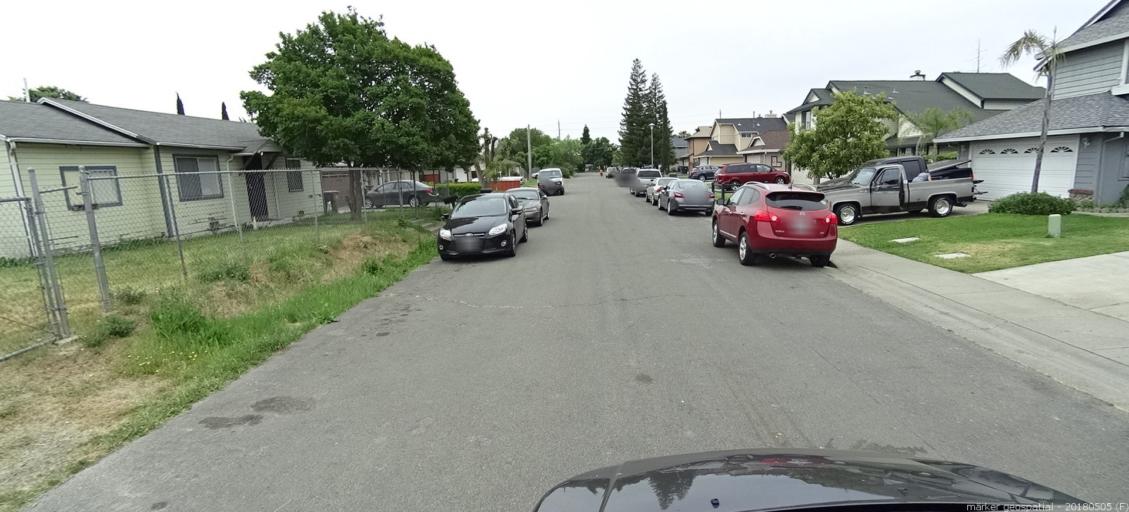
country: US
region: California
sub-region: Sacramento County
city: Rio Linda
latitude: 38.6491
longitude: -121.4407
